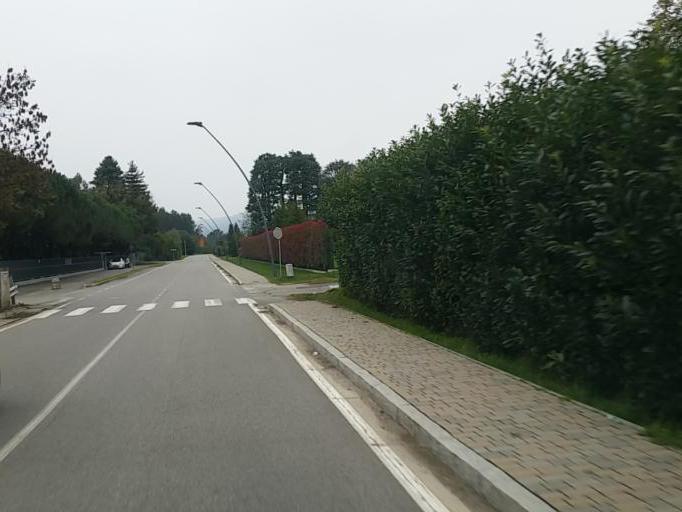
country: IT
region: Piedmont
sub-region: Provincia di Novara
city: Armeno
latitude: 45.8194
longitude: 8.4427
